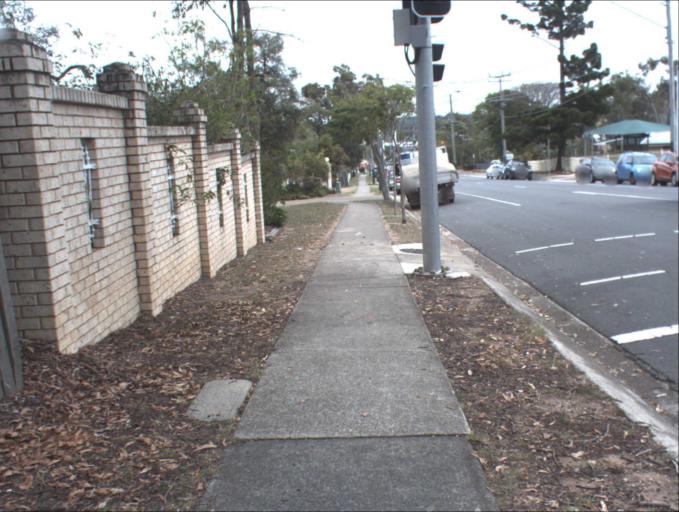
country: AU
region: Queensland
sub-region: Logan
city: Springwood
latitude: -27.6184
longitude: 153.1312
